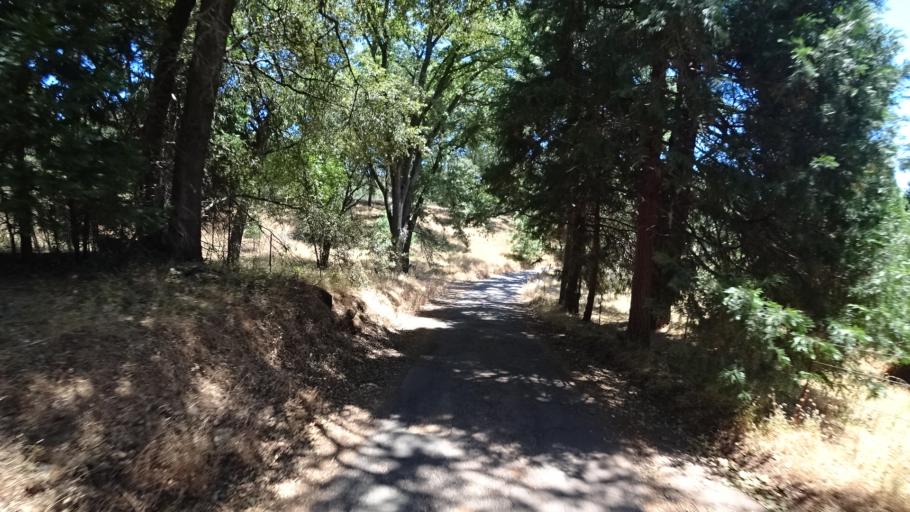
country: US
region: California
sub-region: Calaveras County
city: Mountain Ranch
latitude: 38.2721
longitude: -120.5884
